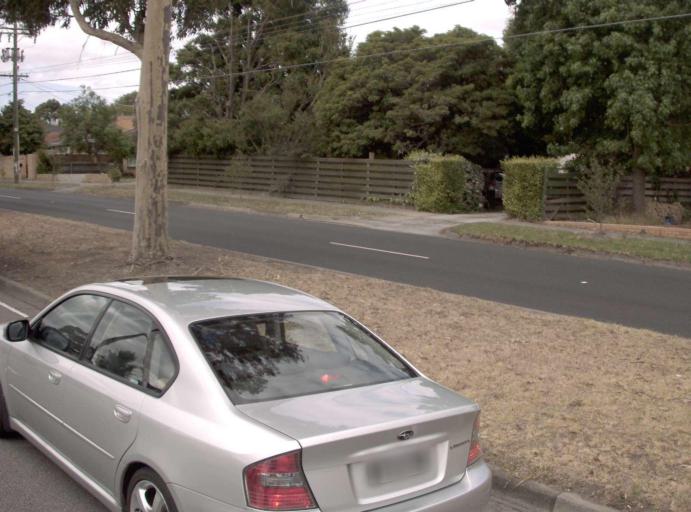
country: AU
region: Victoria
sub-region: Greater Dandenong
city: Dandenong North
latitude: -37.9732
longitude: 145.2230
